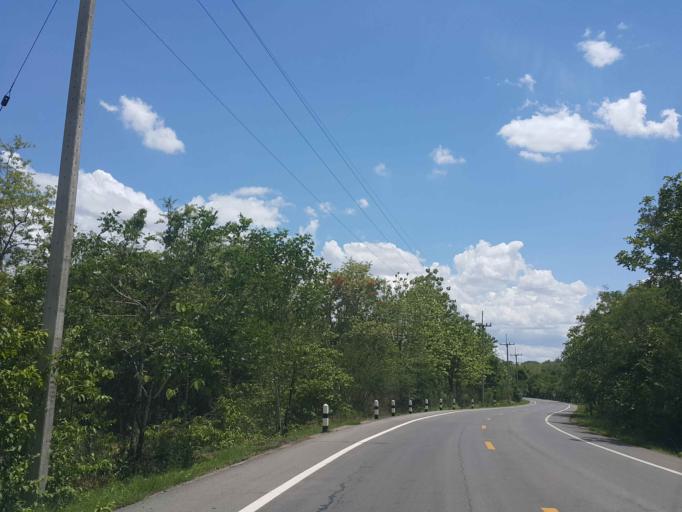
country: TH
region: Phrae
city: Nong Muang Khai
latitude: 18.1922
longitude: 100.2161
